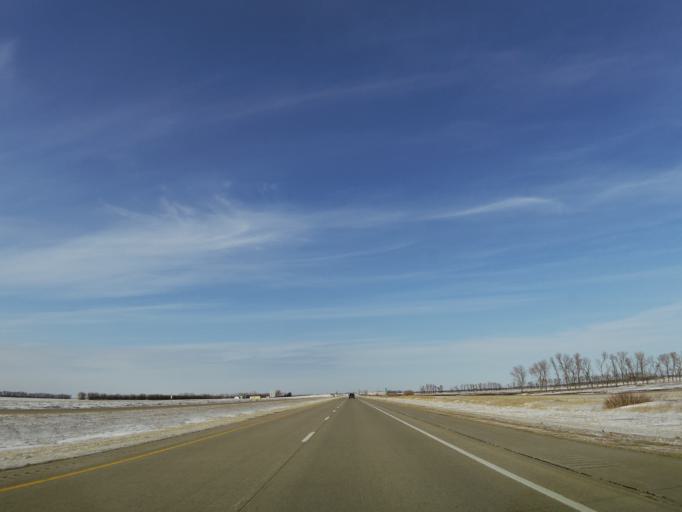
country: US
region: North Dakota
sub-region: Walsh County
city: Grafton
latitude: 48.4284
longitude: -97.1904
